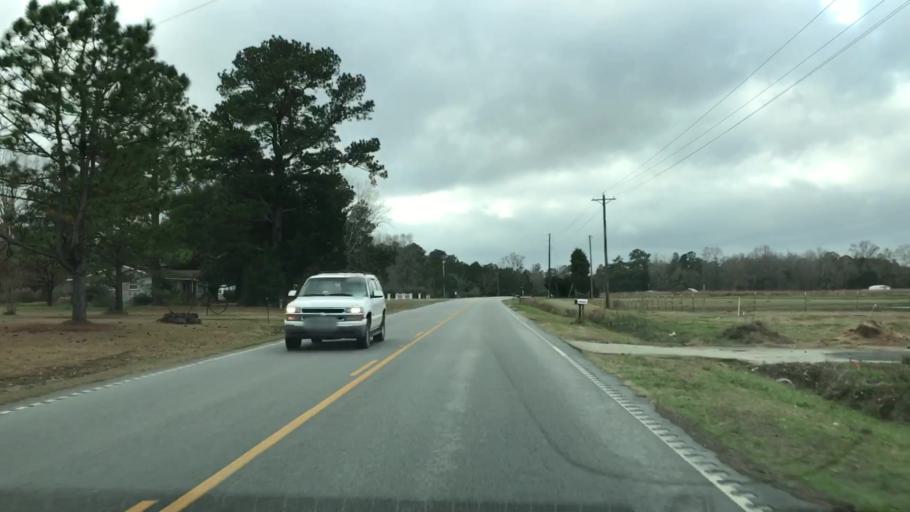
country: US
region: South Carolina
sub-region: Berkeley County
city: Saint Stephen
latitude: 33.2820
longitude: -79.7263
